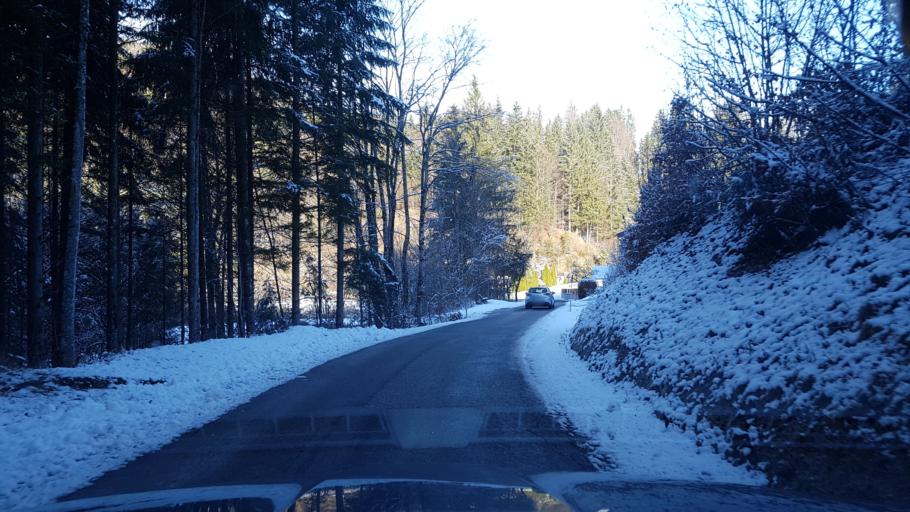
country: AT
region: Salzburg
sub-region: Politischer Bezirk Salzburg-Umgebung
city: Faistenau
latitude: 47.7576
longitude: 13.2343
